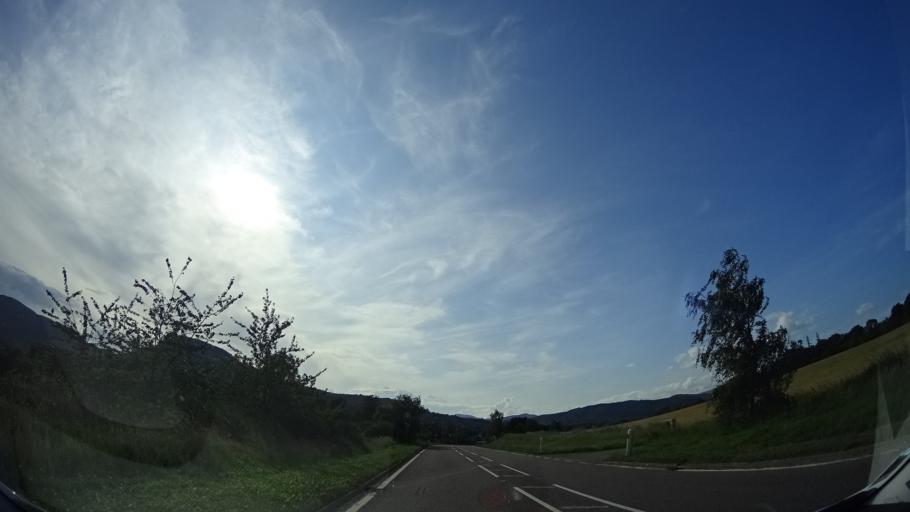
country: GB
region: Scotland
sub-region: Highland
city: Muir of Ord
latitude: 57.5628
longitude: -4.5723
